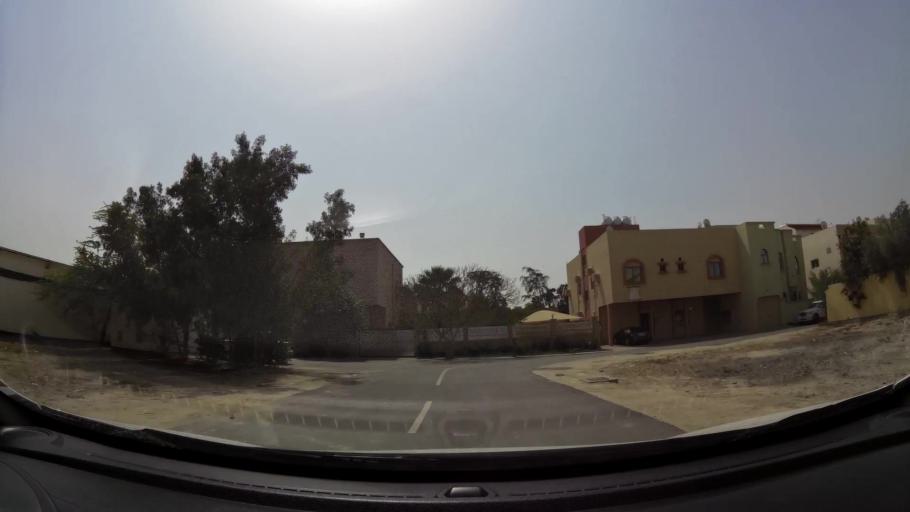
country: BH
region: Manama
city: Jidd Hafs
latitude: 26.2300
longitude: 50.5036
